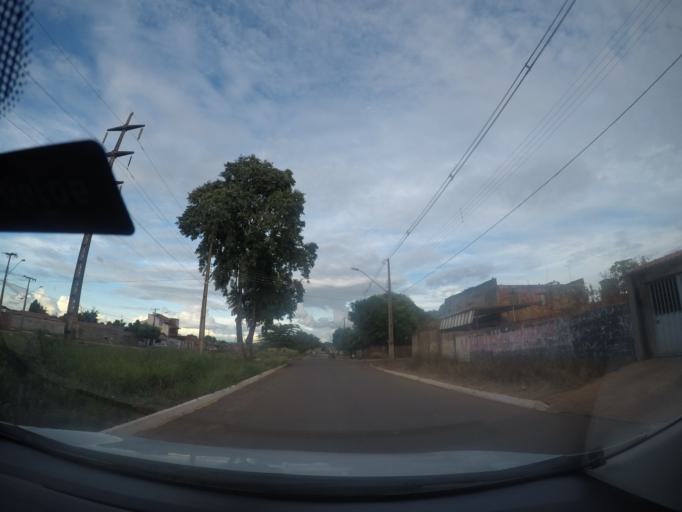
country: BR
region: Goias
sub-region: Goianira
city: Goianira
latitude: -16.5841
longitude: -49.3727
